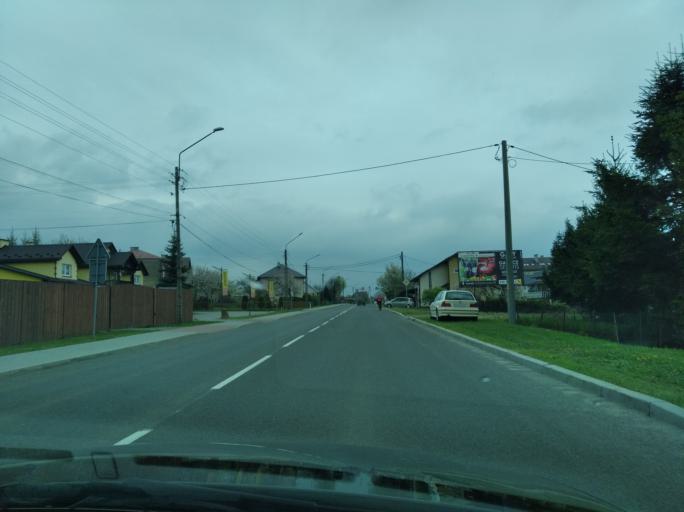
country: PL
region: Subcarpathian Voivodeship
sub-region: Powiat sanocki
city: Sanok
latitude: 49.5503
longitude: 22.2367
